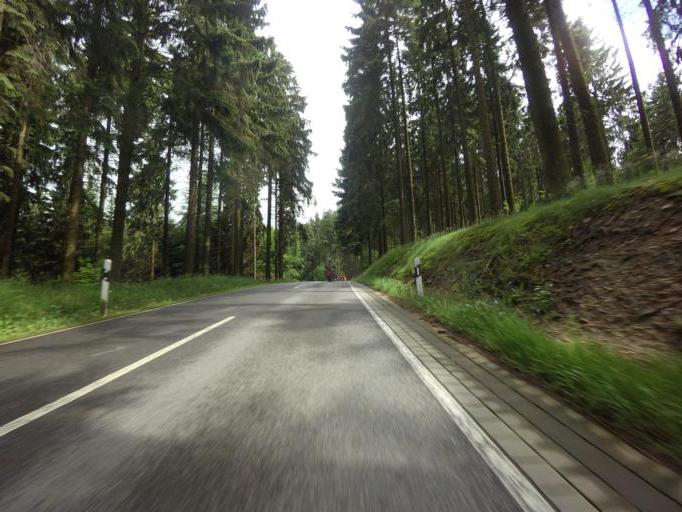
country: DE
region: Rheinland-Pfalz
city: Kaltenborn
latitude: 50.3913
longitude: 7.0073
